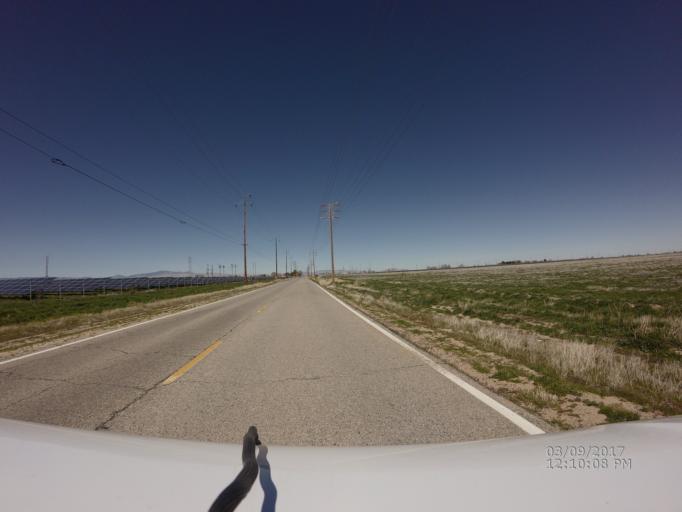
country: US
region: California
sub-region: Los Angeles County
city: Leona Valley
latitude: 34.7118
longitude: -118.2894
